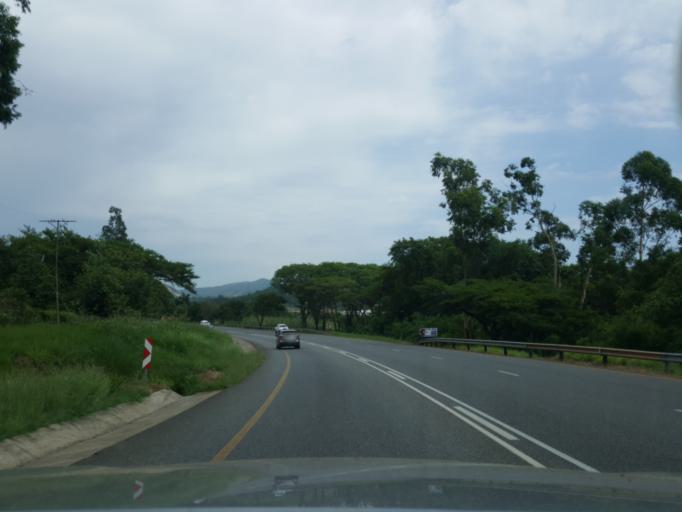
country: ZA
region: Mpumalanga
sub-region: Ehlanzeni District
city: Nelspruit
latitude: -25.4746
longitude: 31.1039
